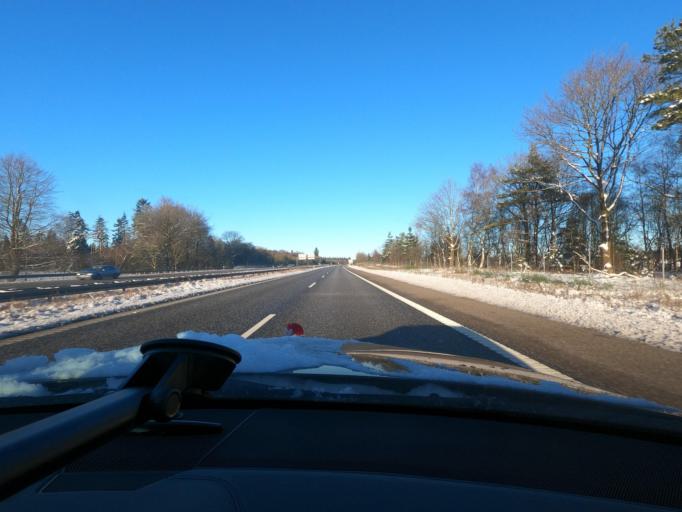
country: DK
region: South Denmark
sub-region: Aabenraa Kommune
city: Aabenraa
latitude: 54.9622
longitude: 9.3837
